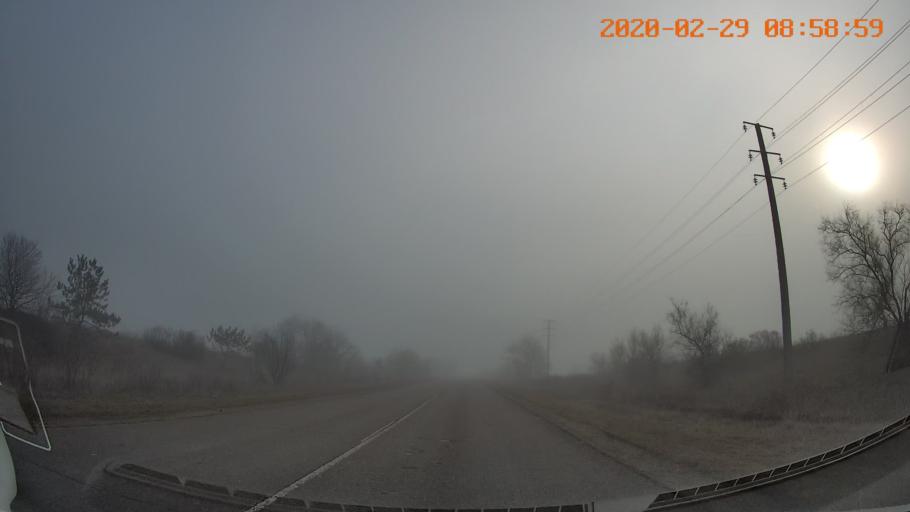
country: MD
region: Telenesti
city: Tiraspolul Nou
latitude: 46.9195
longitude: 29.6511
